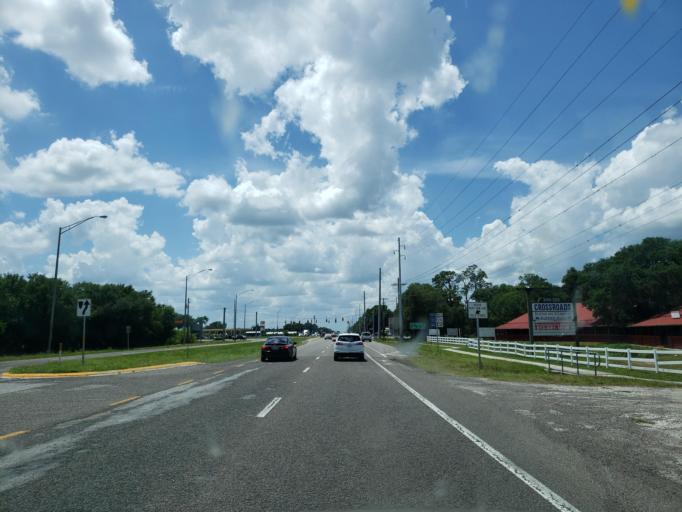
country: US
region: Florida
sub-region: Hillsborough County
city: Plant City
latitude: 27.9378
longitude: -82.1189
